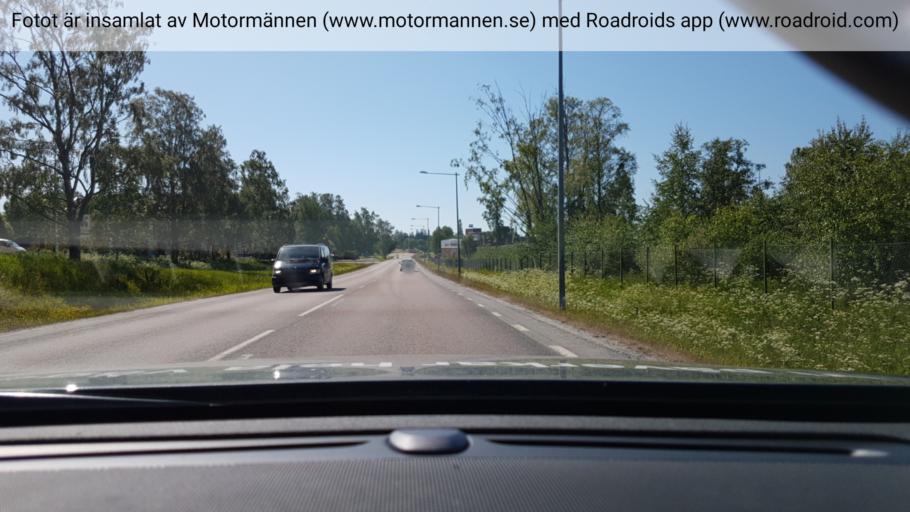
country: SE
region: Vaesterbotten
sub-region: Umea Kommun
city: Holmsund
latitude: 63.7109
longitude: 20.3599
